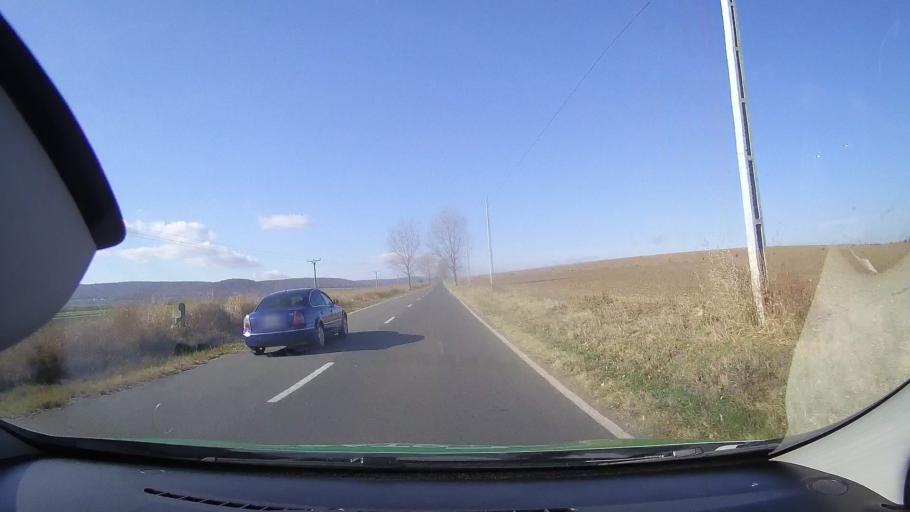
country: RO
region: Tulcea
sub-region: Comuna Sarichioi
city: Enisala
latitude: 44.8790
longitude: 28.7940
